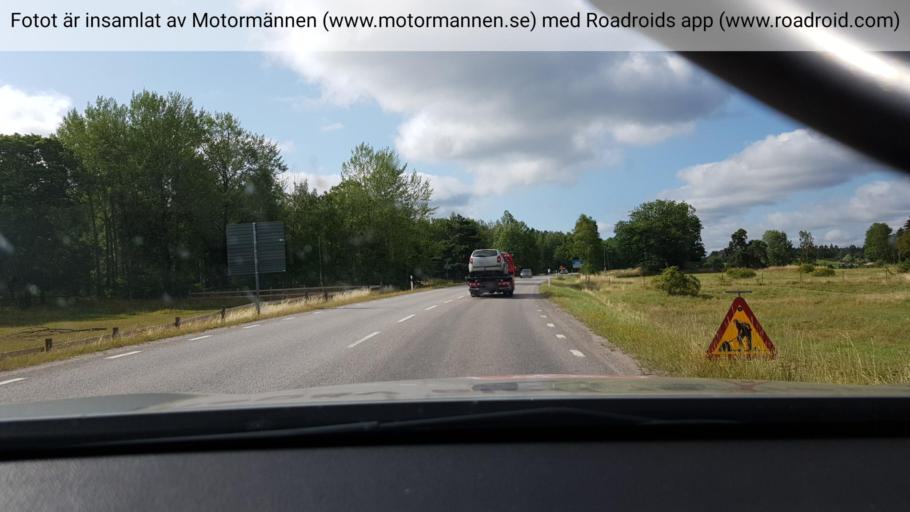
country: SE
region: Uppsala
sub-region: Uppsala Kommun
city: Saevja
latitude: 59.8203
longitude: 17.6987
